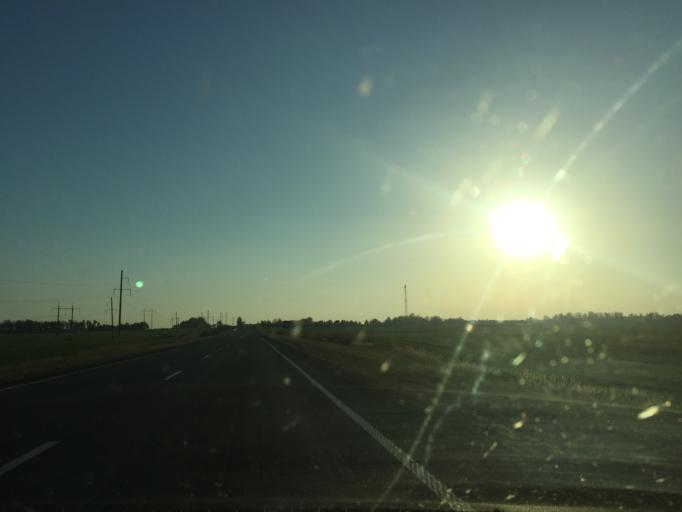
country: BY
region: Mogilev
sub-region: Mahilyowski Rayon
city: Veyno
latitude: 53.8195
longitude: 30.4657
